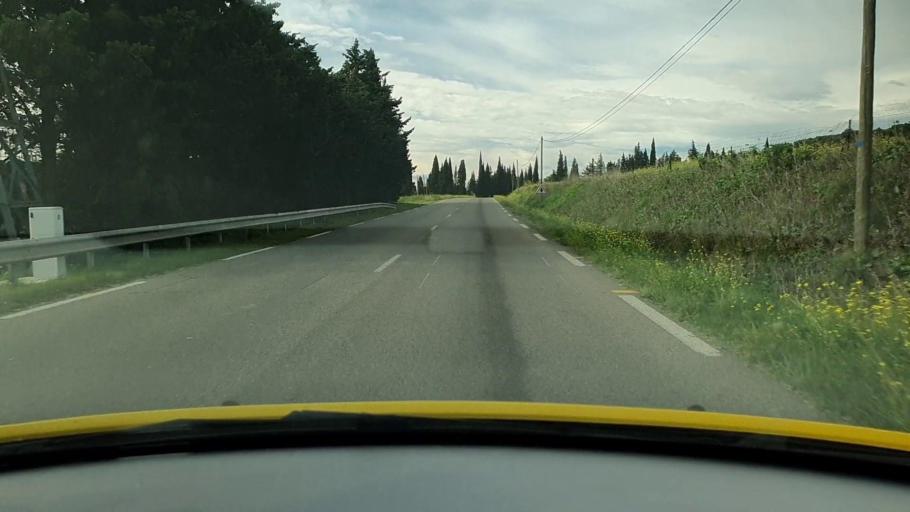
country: FR
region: Languedoc-Roussillon
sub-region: Departement du Gard
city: Bellegarde
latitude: 43.7742
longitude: 4.5384
